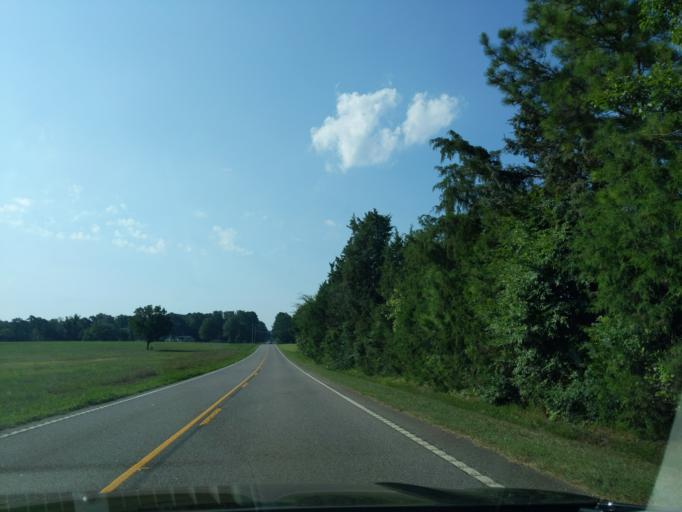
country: US
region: South Carolina
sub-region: Lexington County
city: Leesville
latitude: 34.0596
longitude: -81.5595
